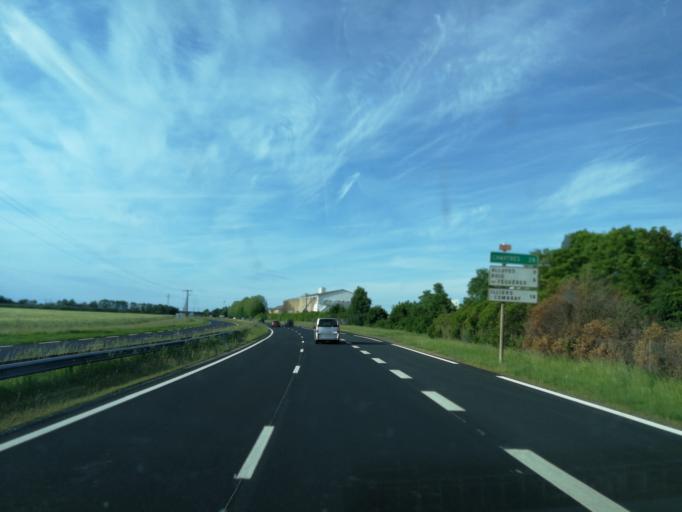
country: FR
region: Centre
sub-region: Departement d'Eure-et-Loir
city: Bonneval
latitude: 48.1965
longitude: 1.3933
